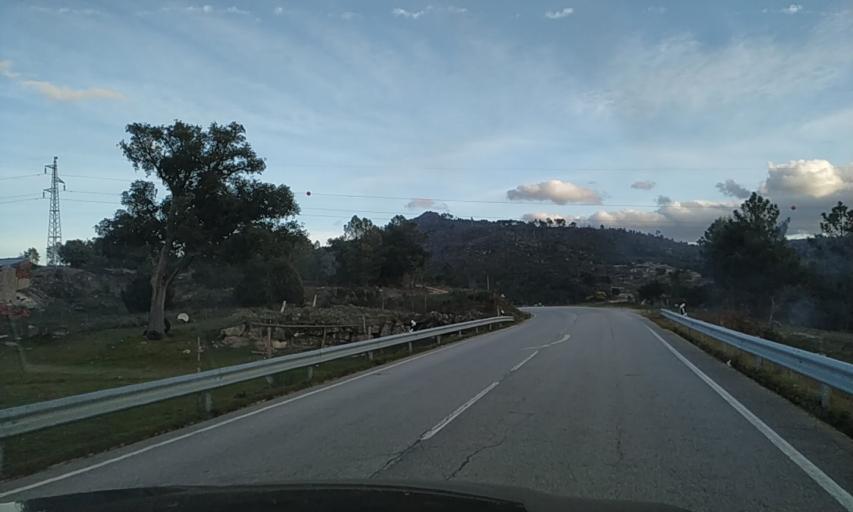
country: PT
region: Braganca
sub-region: Carrazeda de Ansiaes
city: Carrazeda de Anciaes
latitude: 41.2741
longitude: -7.3264
